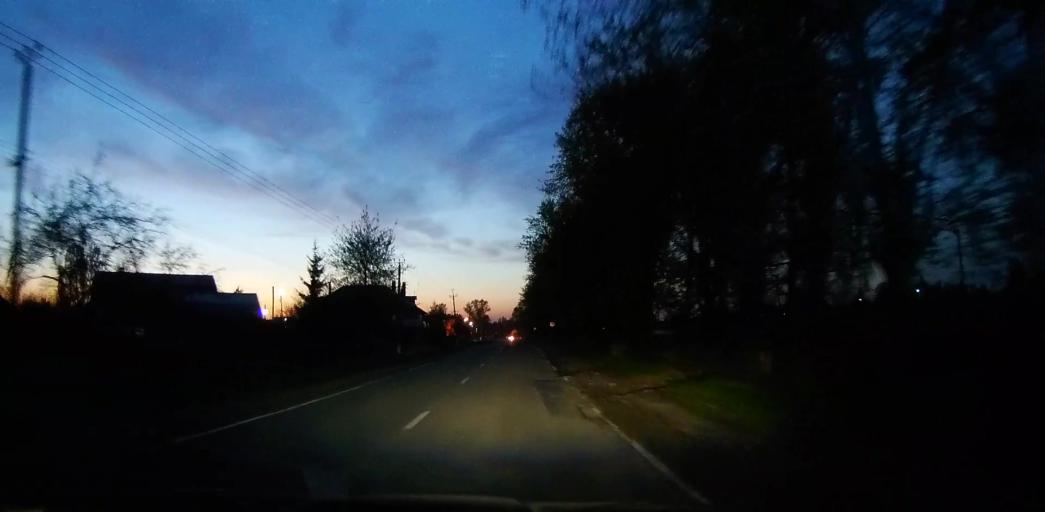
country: RU
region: Moskovskaya
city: Peski
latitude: 55.2126
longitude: 38.7721
